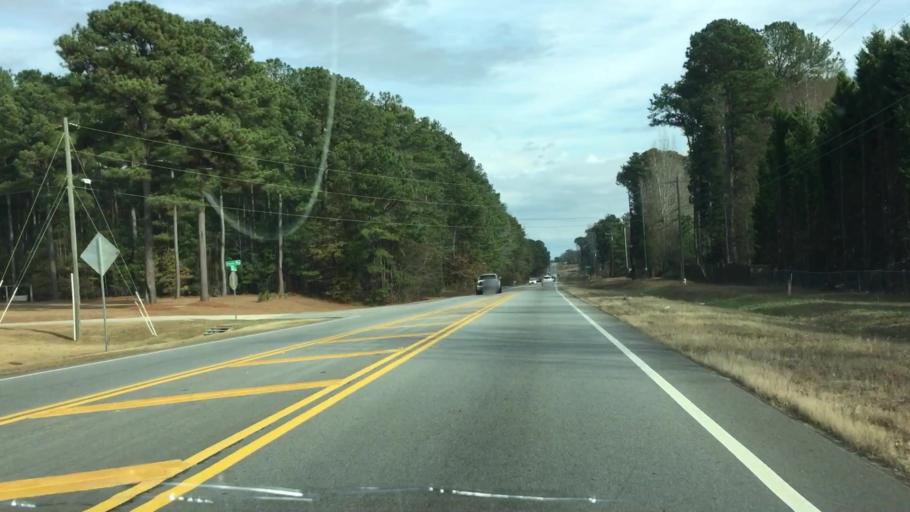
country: US
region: Georgia
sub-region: Henry County
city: McDonough
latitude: 33.4309
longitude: -84.0591
